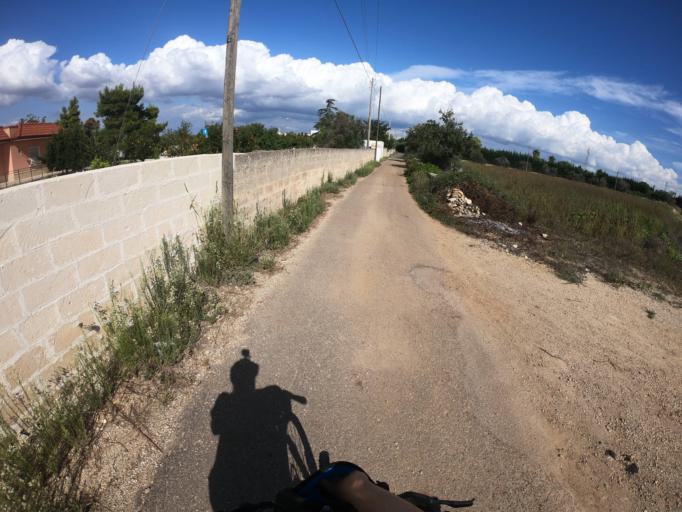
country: IT
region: Apulia
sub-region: Provincia di Lecce
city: Galatone
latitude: 40.1436
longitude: 18.0514
